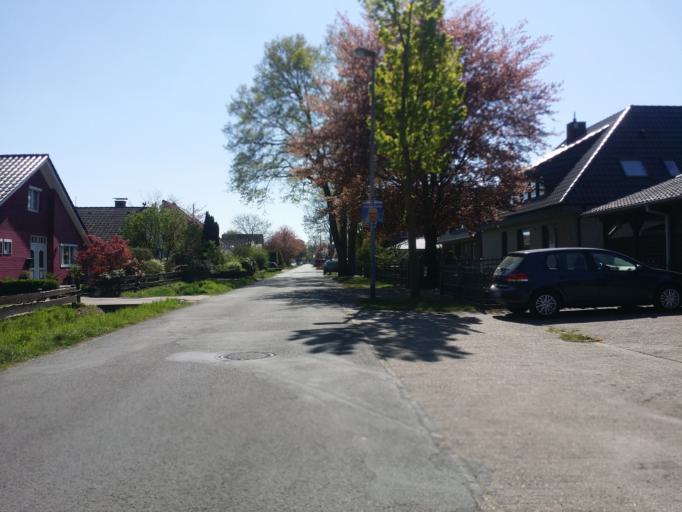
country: DE
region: Lower Saxony
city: Delmenhorst
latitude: 53.0327
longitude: 8.6889
